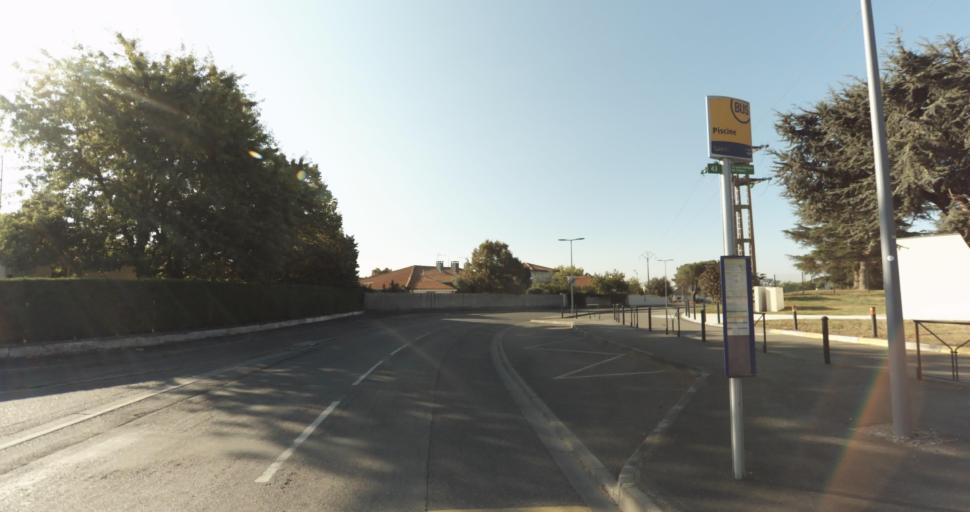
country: FR
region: Midi-Pyrenees
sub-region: Departement de la Haute-Garonne
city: L'Union
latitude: 43.6553
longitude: 1.4916
